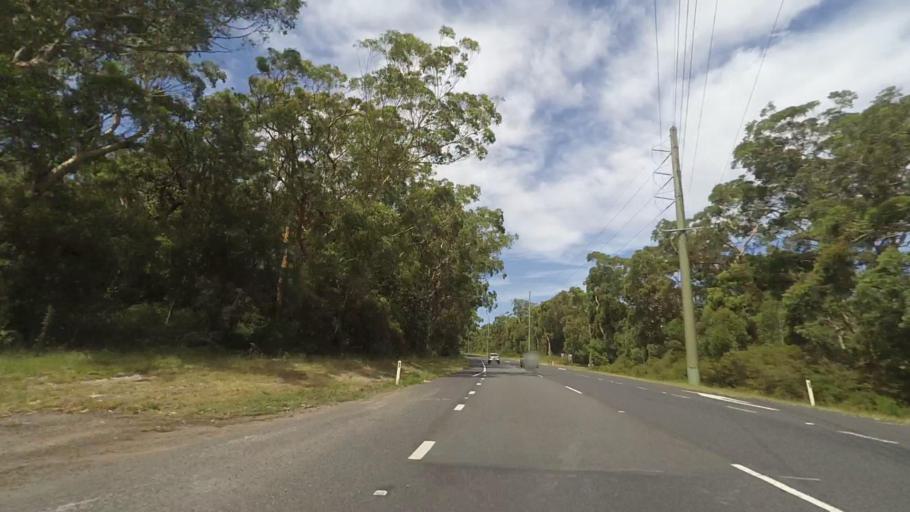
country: AU
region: New South Wales
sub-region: Port Stephens Shire
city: Anna Bay
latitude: -32.7837
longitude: 151.9788
